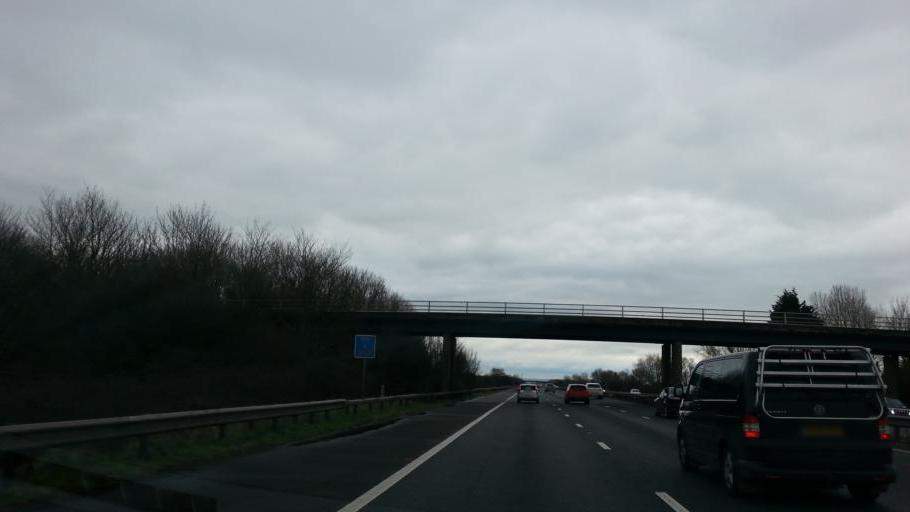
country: GB
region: England
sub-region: Somerset
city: Highbridge
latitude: 51.2075
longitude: -2.9654
